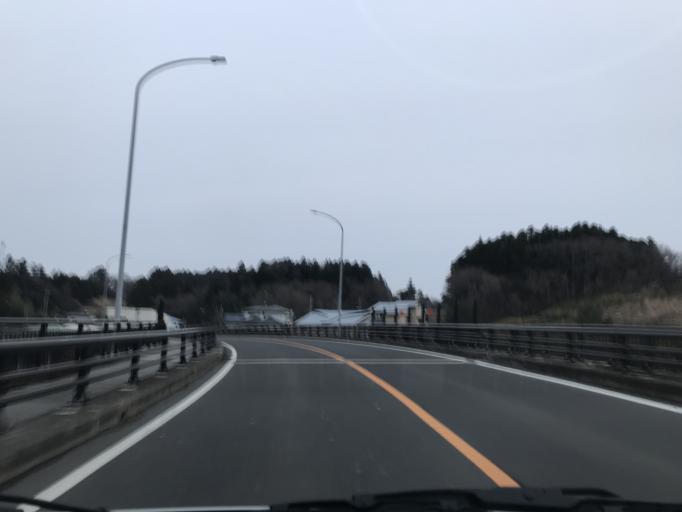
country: JP
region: Miyagi
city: Wakuya
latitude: 38.7076
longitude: 141.1133
